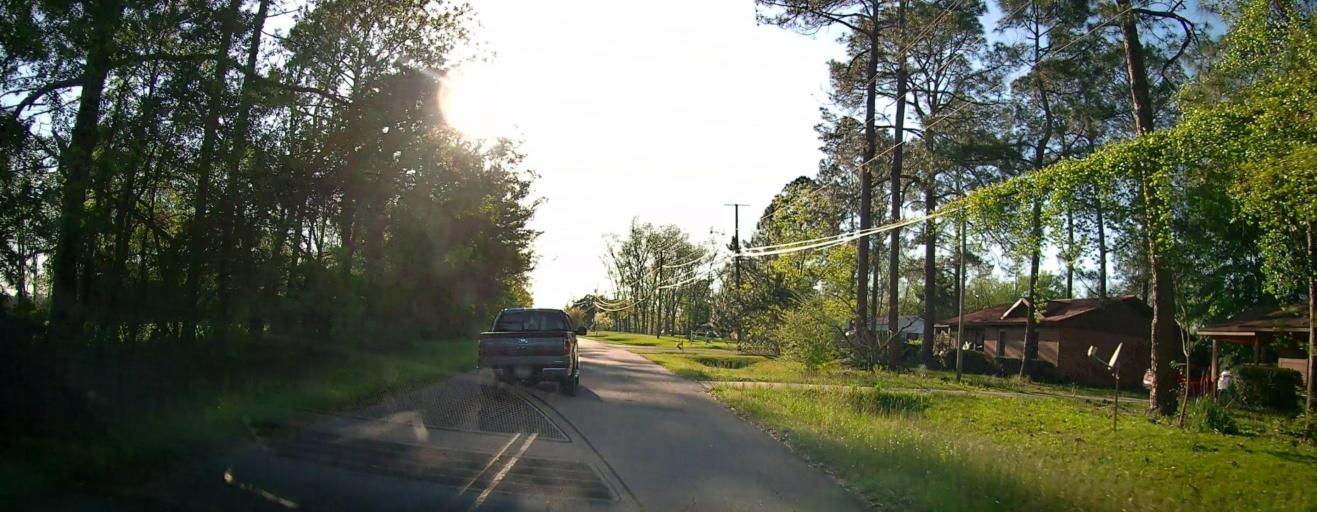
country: US
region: Georgia
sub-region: Ben Hill County
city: Fitzgerald
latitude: 31.7066
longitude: -83.2320
